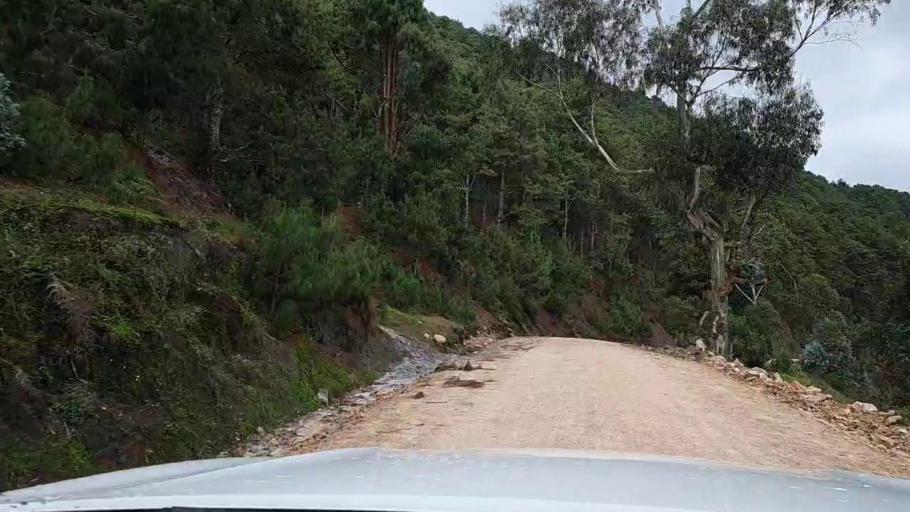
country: RW
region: Southern Province
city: Nzega
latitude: -2.3039
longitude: 29.3834
